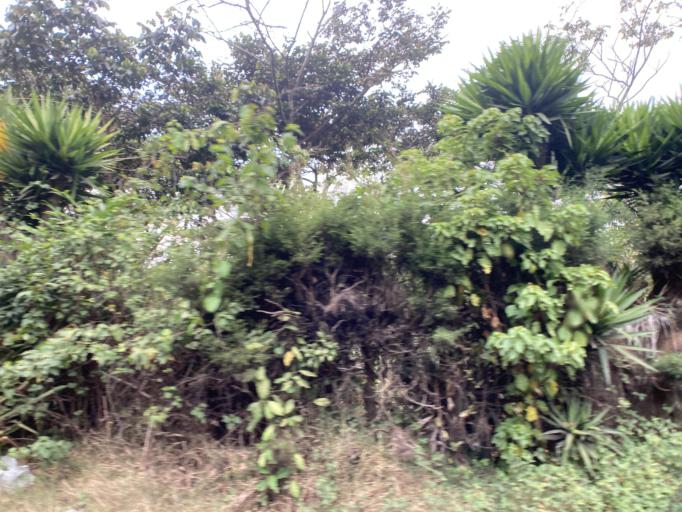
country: GT
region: Guatemala
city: Villa Canales
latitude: 14.4168
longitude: -90.5305
